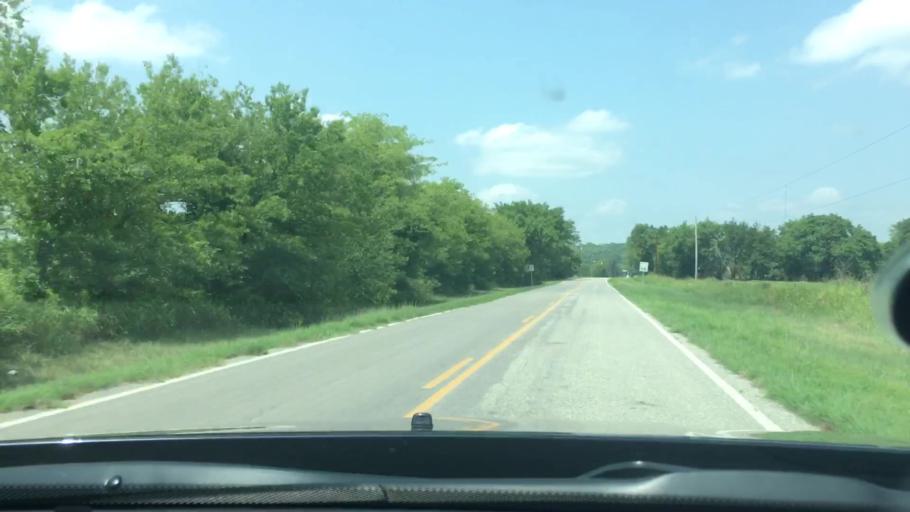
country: US
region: Oklahoma
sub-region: Johnston County
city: Tishomingo
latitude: 34.4103
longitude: -96.4968
